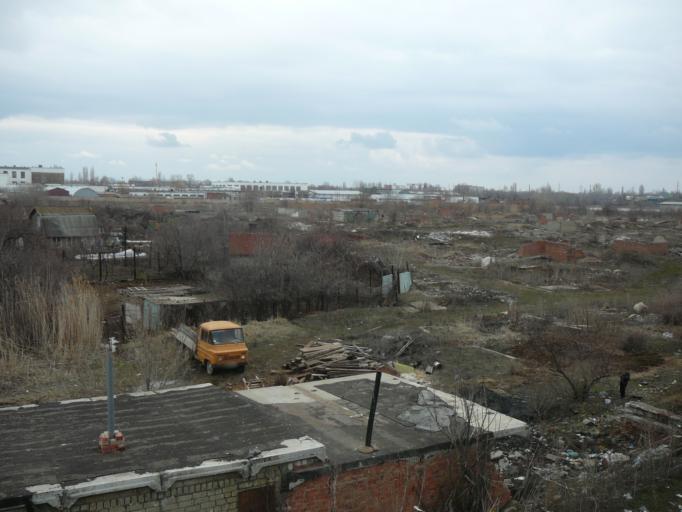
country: RU
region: Saratov
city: Engel's
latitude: 51.4637
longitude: 46.0967
